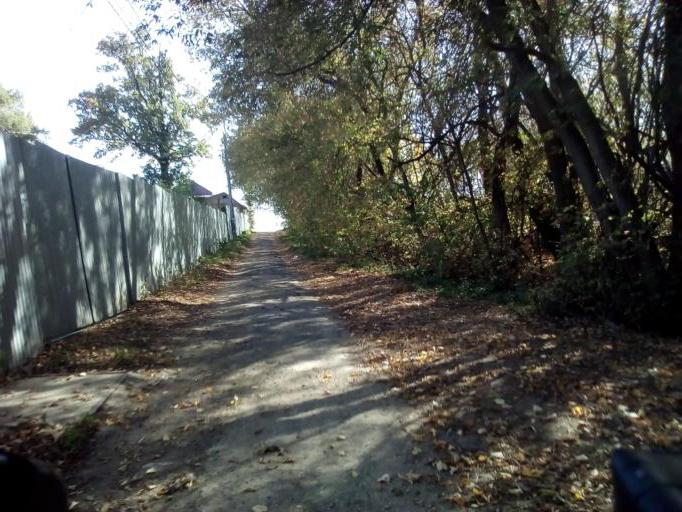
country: RU
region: Moskovskaya
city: Ramenskoye
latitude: 55.5445
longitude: 38.2928
